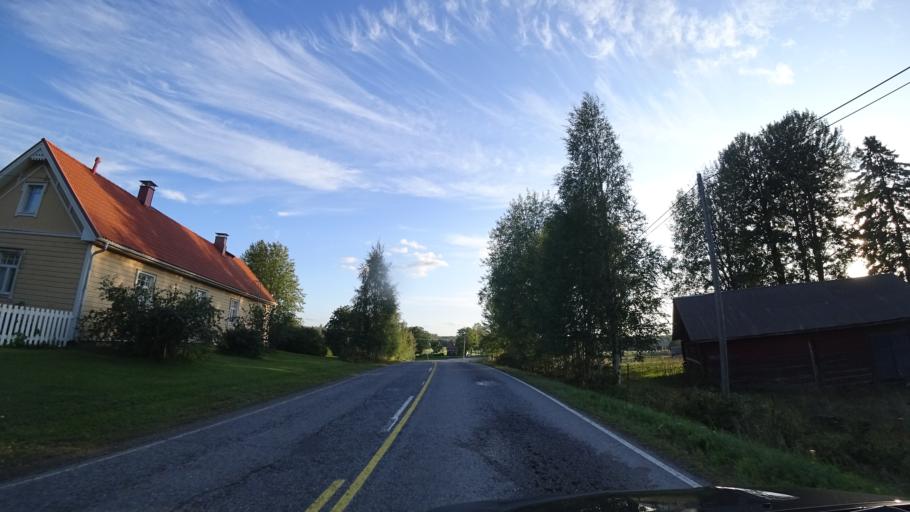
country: FI
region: Haeme
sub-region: Haemeenlinna
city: Lammi
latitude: 61.0447
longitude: 24.9400
